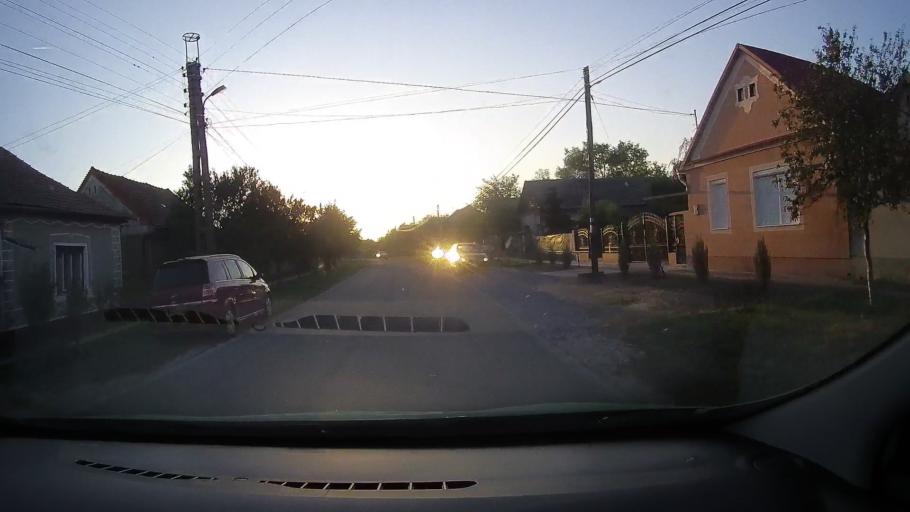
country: RO
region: Bihor
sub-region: Comuna Rosiori
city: Rosiori
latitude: 47.2562
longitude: 21.9574
